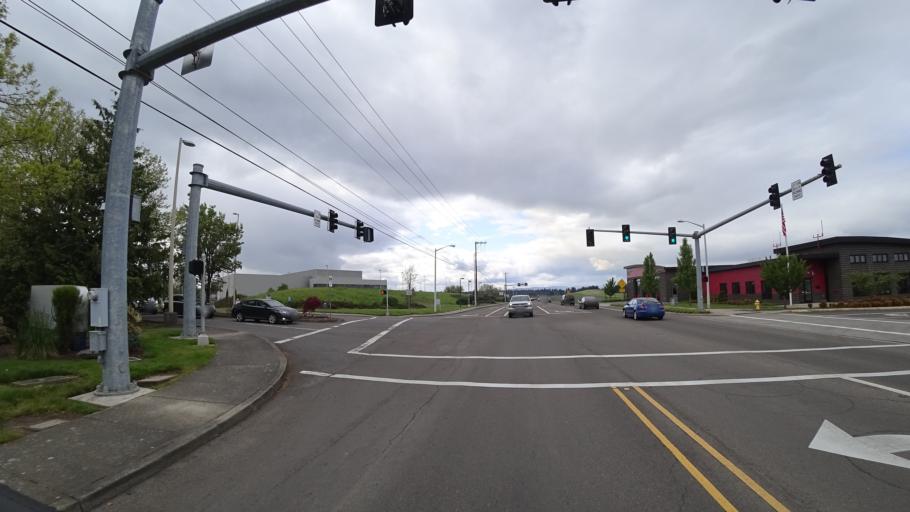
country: US
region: Oregon
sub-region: Washington County
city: Hillsboro
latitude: 45.5453
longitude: -122.9589
